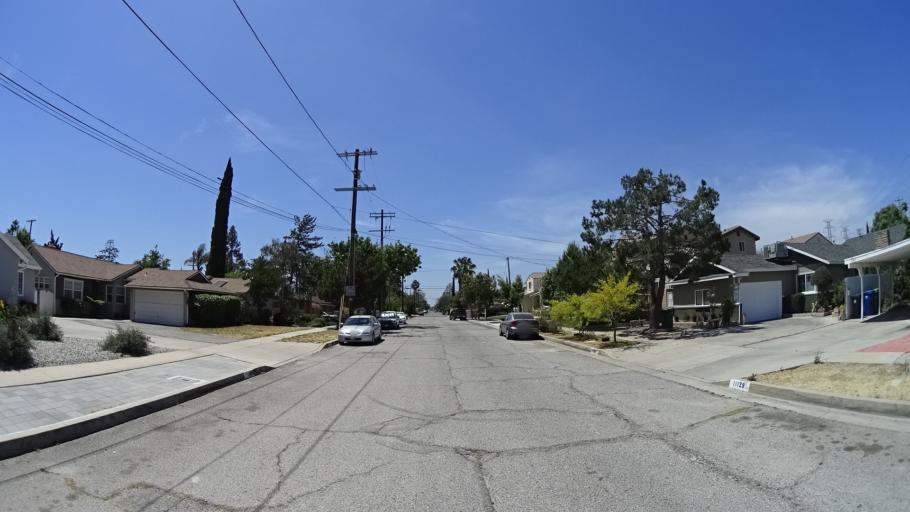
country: US
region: California
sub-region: Los Angeles County
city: North Hollywood
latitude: 34.1849
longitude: -118.3735
